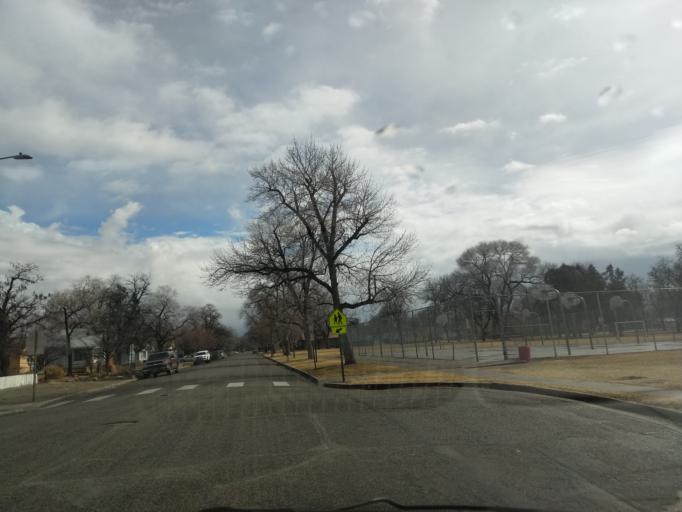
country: US
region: Colorado
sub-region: Mesa County
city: Grand Junction
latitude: 39.0745
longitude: -108.5579
